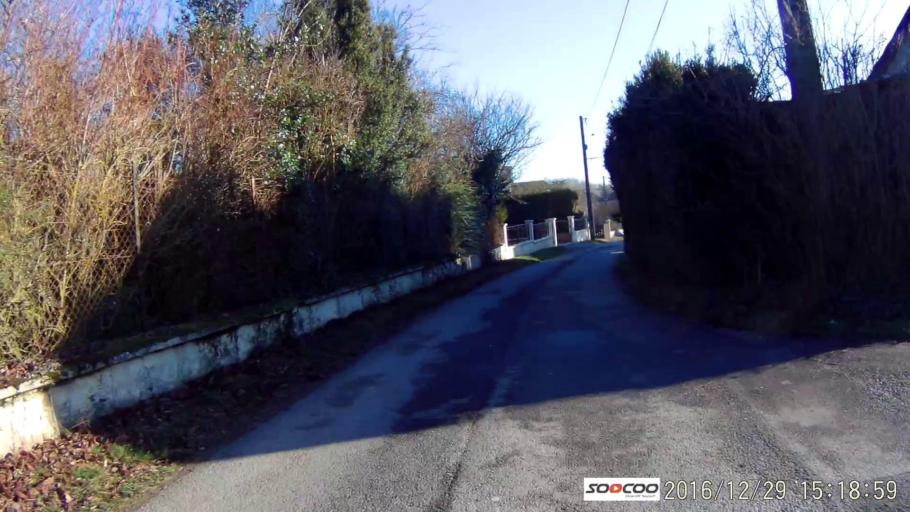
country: FR
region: Centre
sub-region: Departement de l'Indre
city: Neuvy-Pailloux
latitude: 46.9394
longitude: 1.8028
